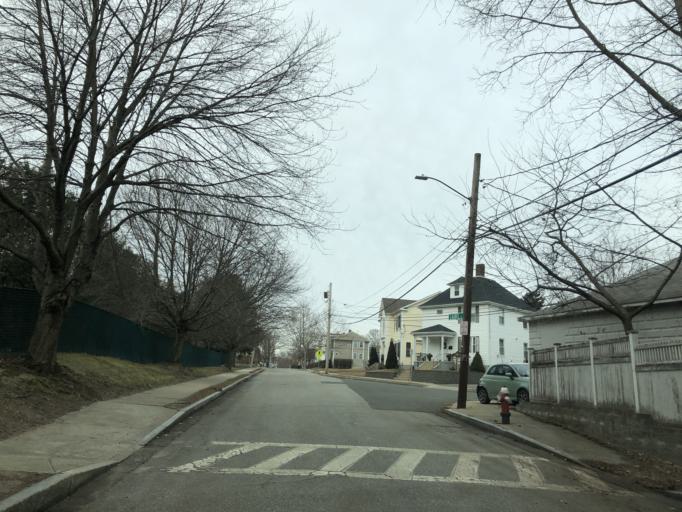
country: US
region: Massachusetts
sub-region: Middlesex County
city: Watertown
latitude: 42.3662
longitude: -71.1606
